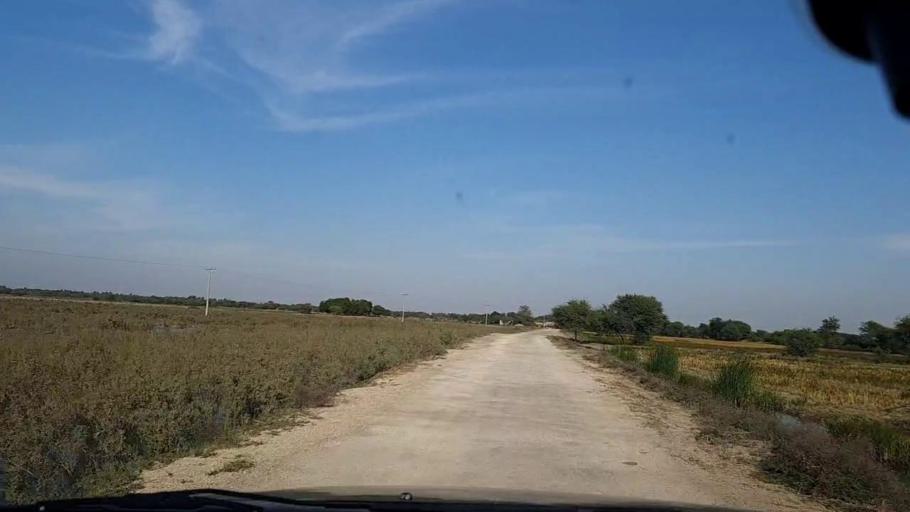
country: PK
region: Sindh
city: Mirpur Batoro
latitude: 24.6335
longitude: 68.2992
